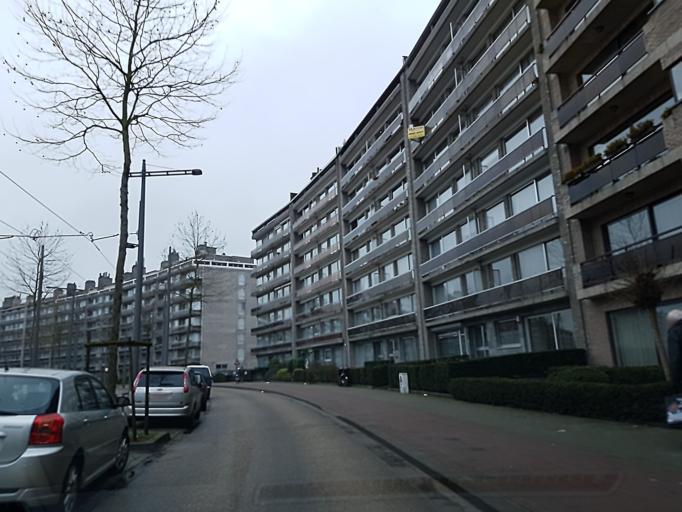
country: BE
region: Flanders
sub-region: Provincie Antwerpen
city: Borsbeek
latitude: 51.2025
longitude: 4.4688
